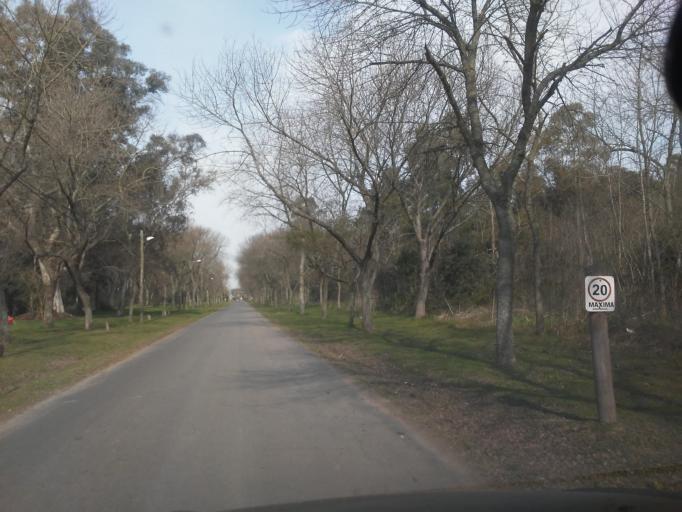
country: AR
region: Buenos Aires
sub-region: Partido de General Rodriguez
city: General Rodriguez
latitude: -34.6673
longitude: -58.8590
